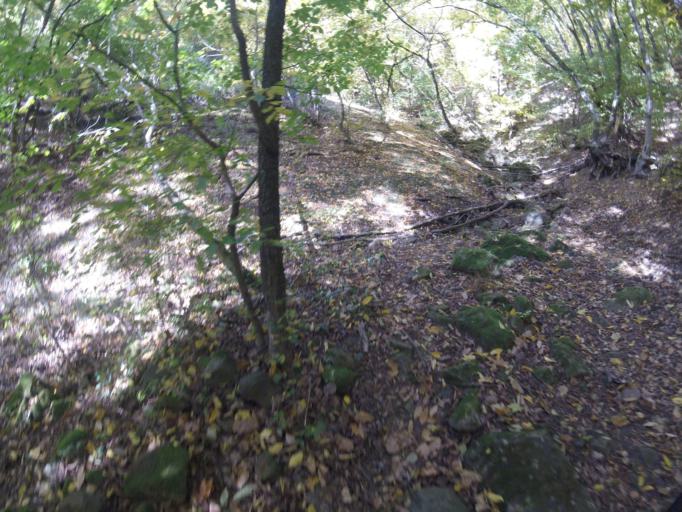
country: HU
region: Pest
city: Csobanka
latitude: 47.6438
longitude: 18.9449
